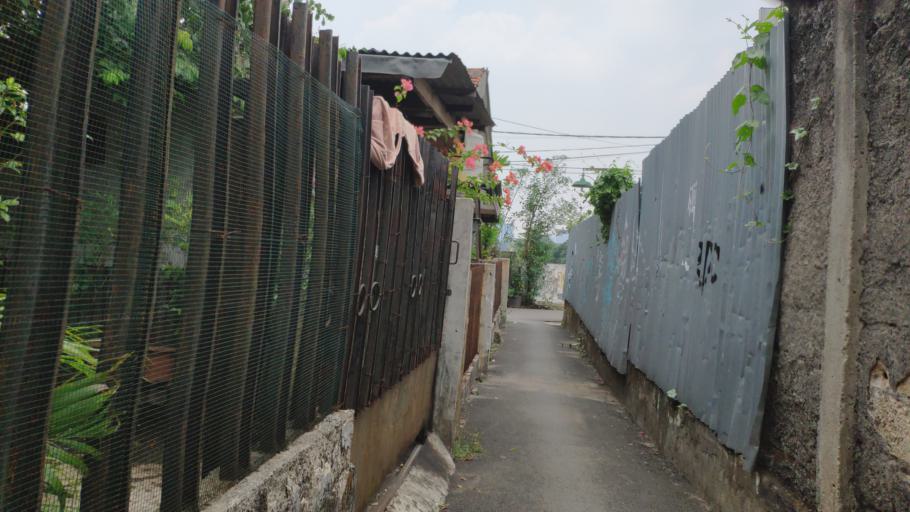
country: ID
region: Jakarta Raya
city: Jakarta
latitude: -6.2675
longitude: 106.7922
